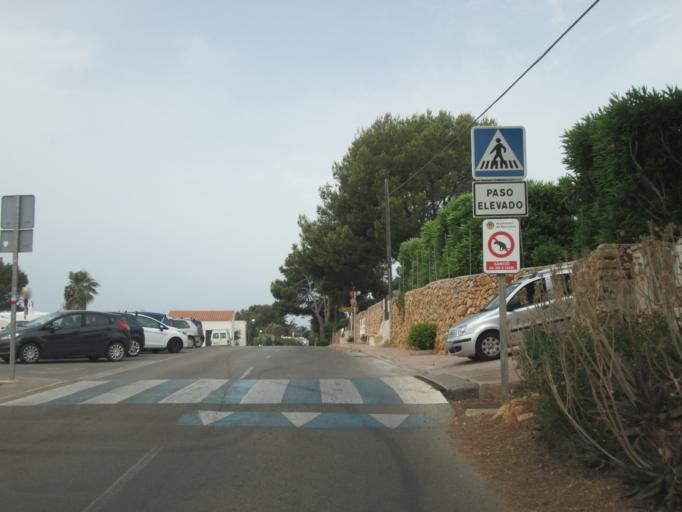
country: ES
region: Balearic Islands
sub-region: Illes Balears
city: Sant Lluis
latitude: 39.8294
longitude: 4.2178
